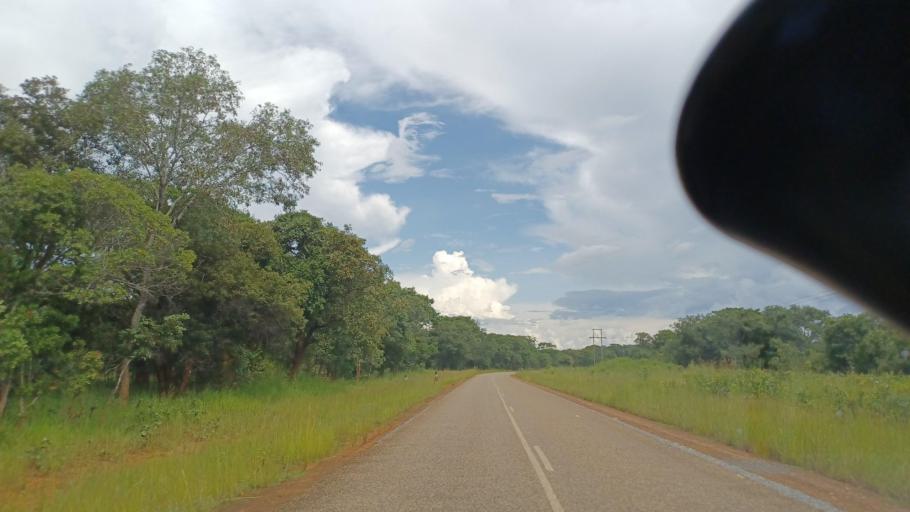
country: ZM
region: North-Western
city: Kasempa
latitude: -13.1583
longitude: 25.8806
